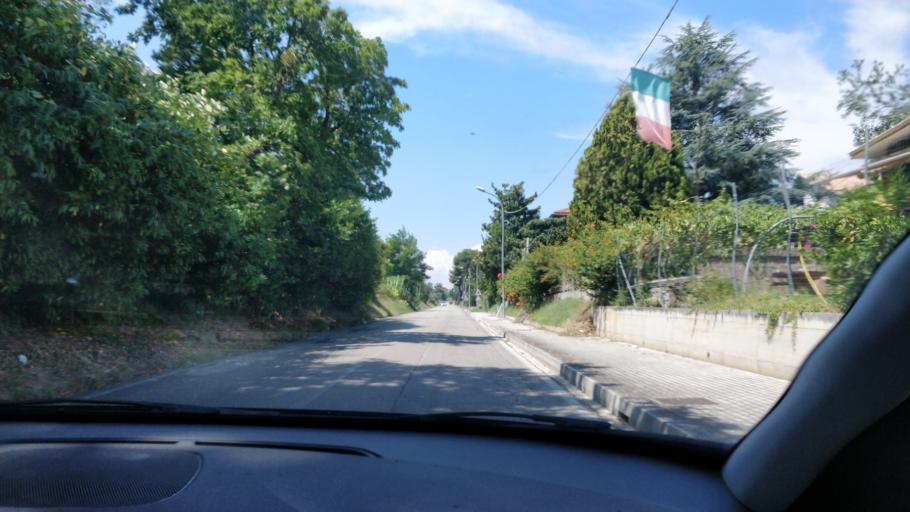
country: IT
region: Abruzzo
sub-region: Provincia di Chieti
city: Francavilla al Mare
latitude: 42.4227
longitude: 14.2645
